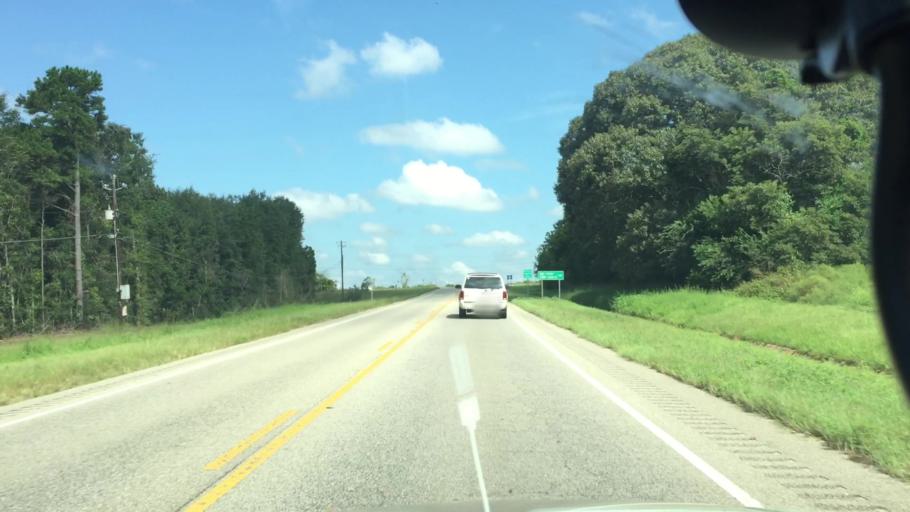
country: US
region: Alabama
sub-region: Coffee County
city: New Brockton
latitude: 31.4134
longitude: -85.8844
